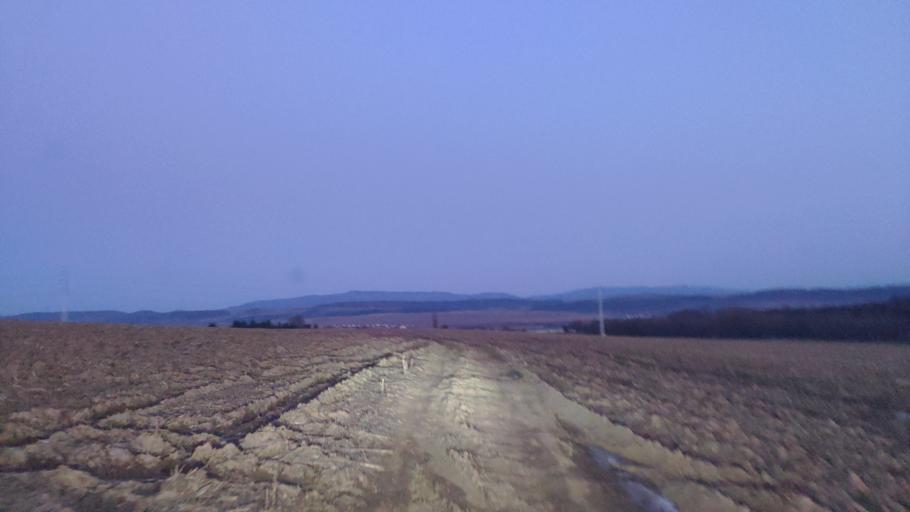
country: SK
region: Kosicky
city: Kosice
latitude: 48.8239
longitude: 21.2809
